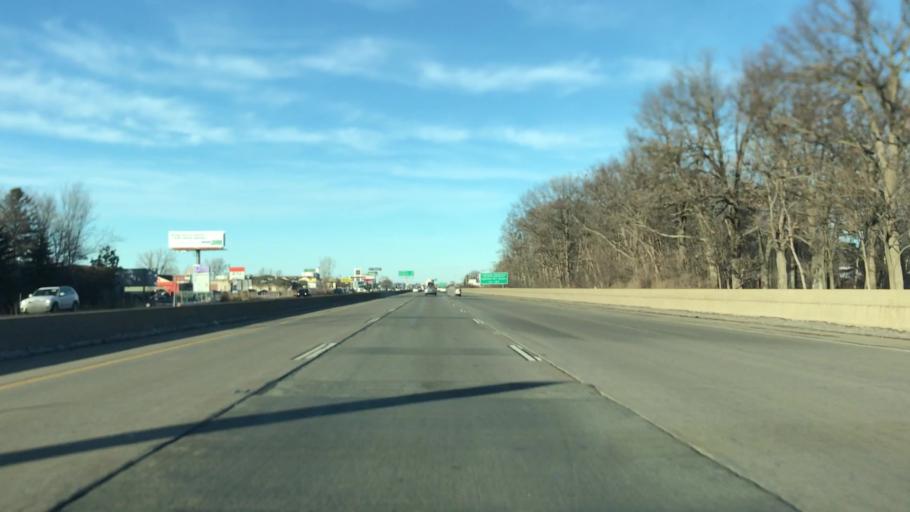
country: US
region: Wisconsin
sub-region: Winnebago County
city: Menasha
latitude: 44.2484
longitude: -88.4663
